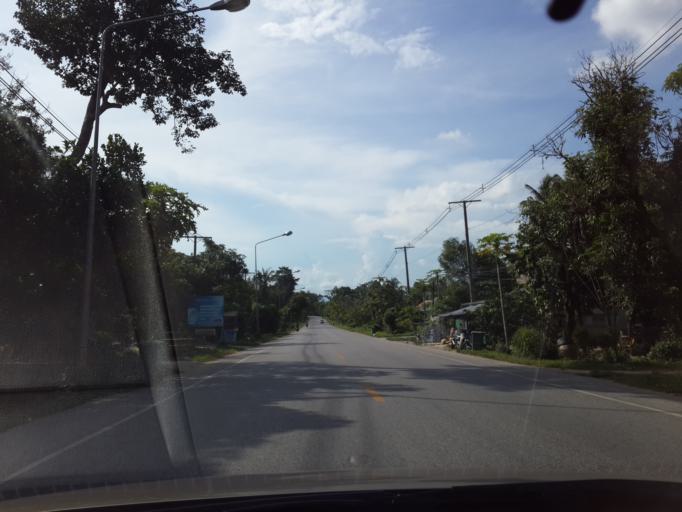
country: TH
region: Yala
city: Yala
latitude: 6.4944
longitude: 101.3017
